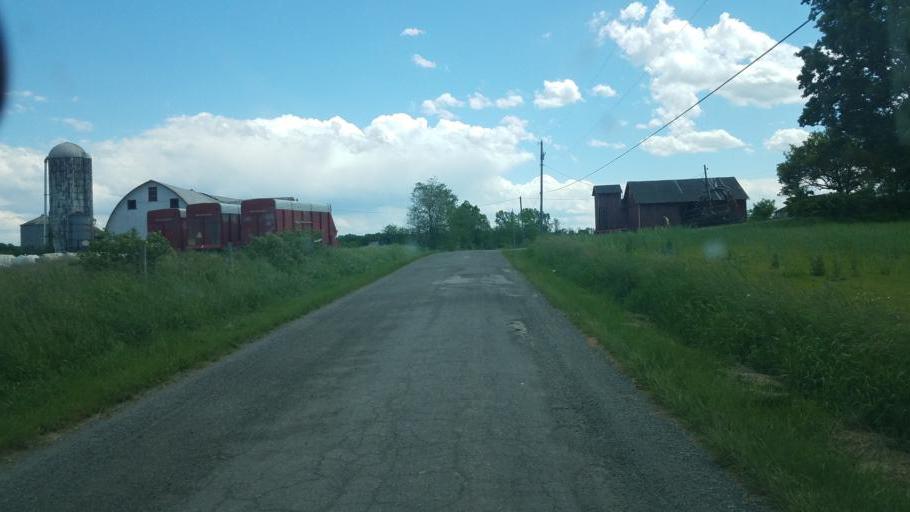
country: US
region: Ohio
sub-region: Geauga County
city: Middlefield
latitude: 41.3895
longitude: -80.9900
